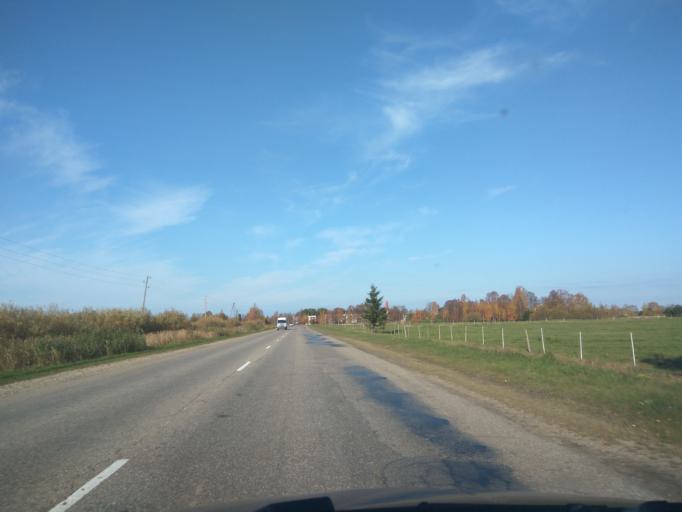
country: LV
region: Ventspils
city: Ventspils
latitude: 57.2986
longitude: 21.5622
